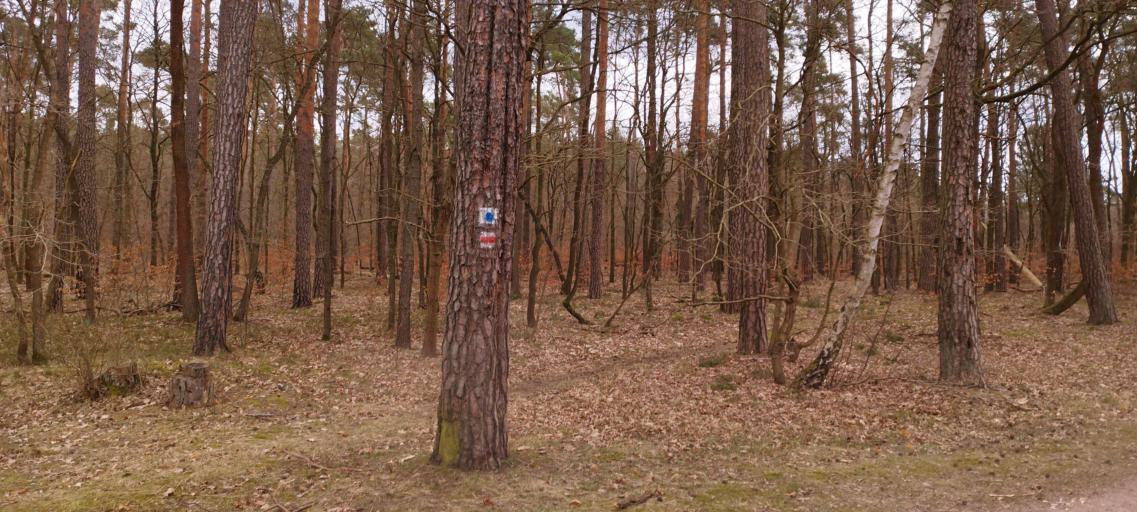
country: DE
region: Brandenburg
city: Erkner
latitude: 52.4150
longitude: 13.7727
